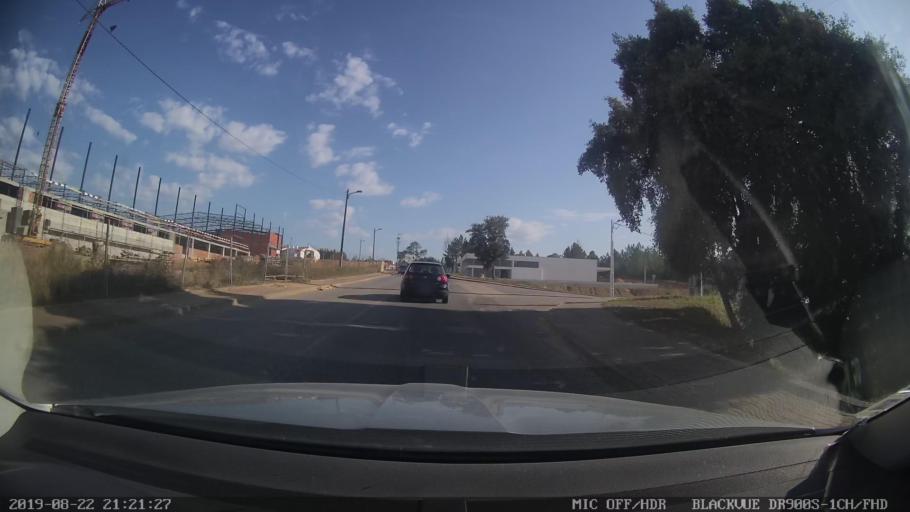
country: PT
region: Castelo Branco
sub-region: Serta
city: Serta
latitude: 39.8186
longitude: -8.1085
